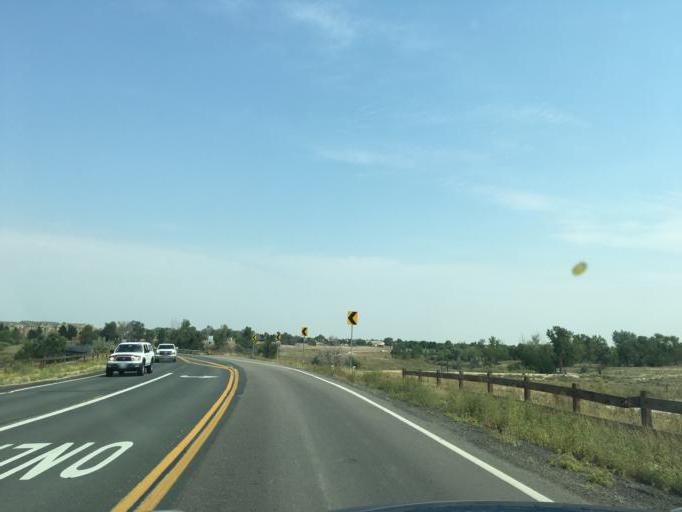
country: US
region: Colorado
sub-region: Adams County
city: Northglenn
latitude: 39.9213
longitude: -105.0135
